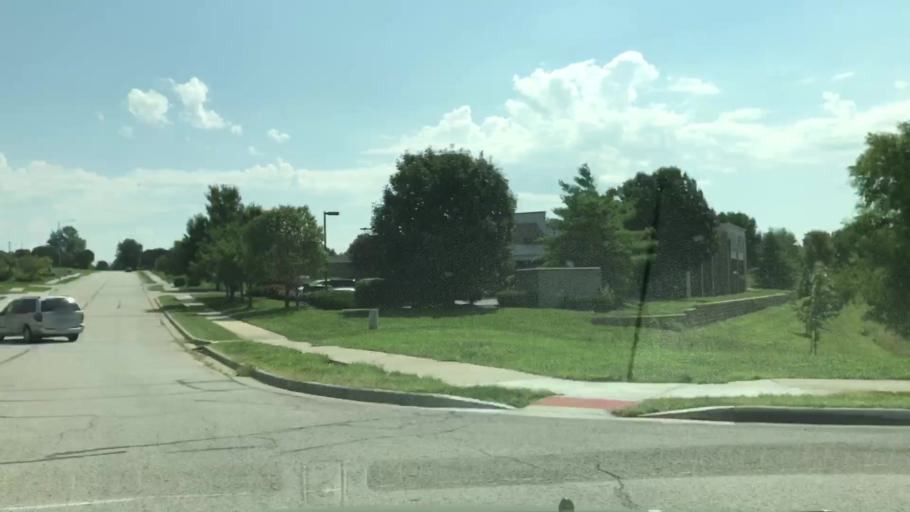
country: US
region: Missouri
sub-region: Cass County
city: Lake Winnebago
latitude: 38.8522
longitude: -94.3987
